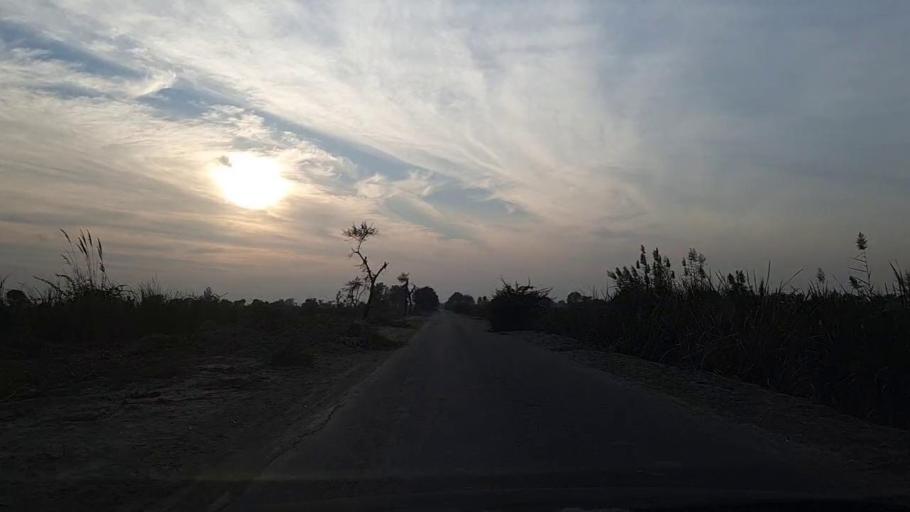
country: PK
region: Sindh
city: Daur
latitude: 26.3989
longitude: 68.4594
